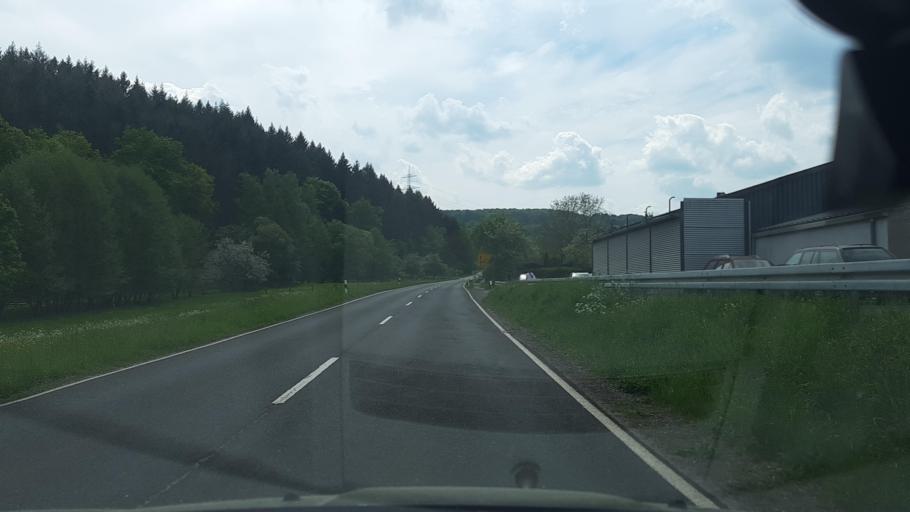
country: DE
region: Hesse
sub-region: Regierungsbezirk Giessen
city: Greifenstein
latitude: 50.6121
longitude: 8.3296
